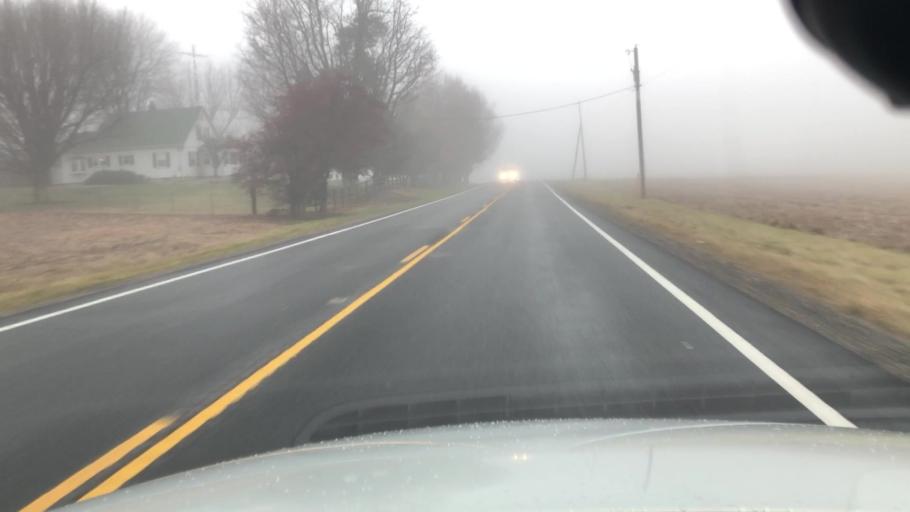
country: US
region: Ohio
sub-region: Logan County
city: Russells Point
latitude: 40.5684
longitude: -83.8452
